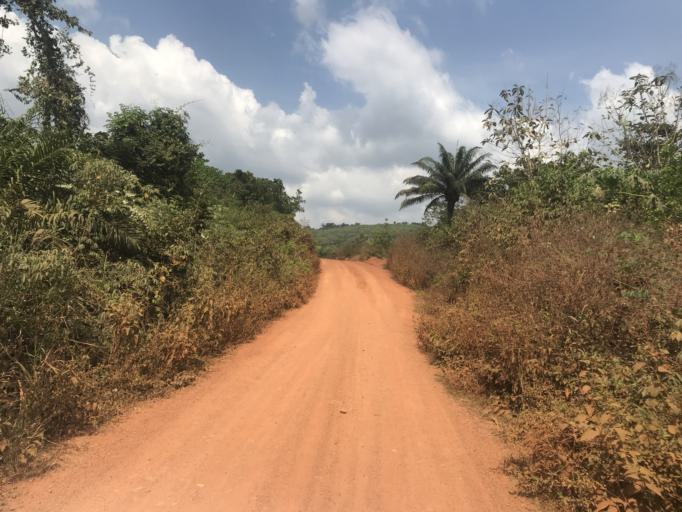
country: NG
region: Osun
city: Inisa
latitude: 7.8947
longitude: 4.3995
